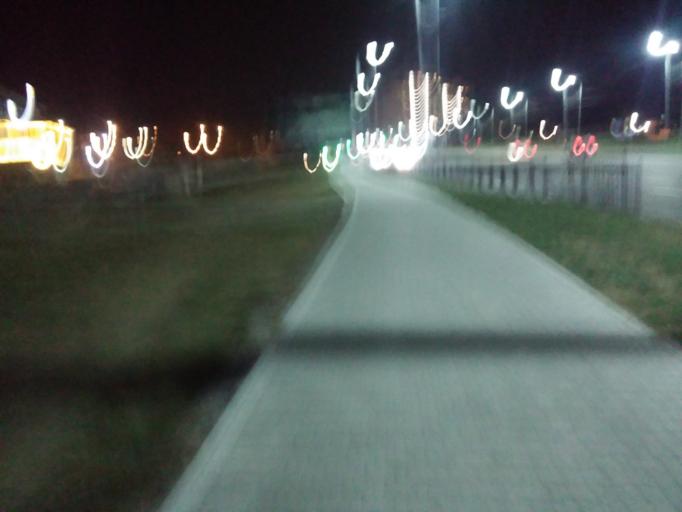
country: RU
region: Khabarovsk Krai
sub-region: Khabarovskiy Rayon
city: Khabarovsk
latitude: 48.4535
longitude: 135.0960
